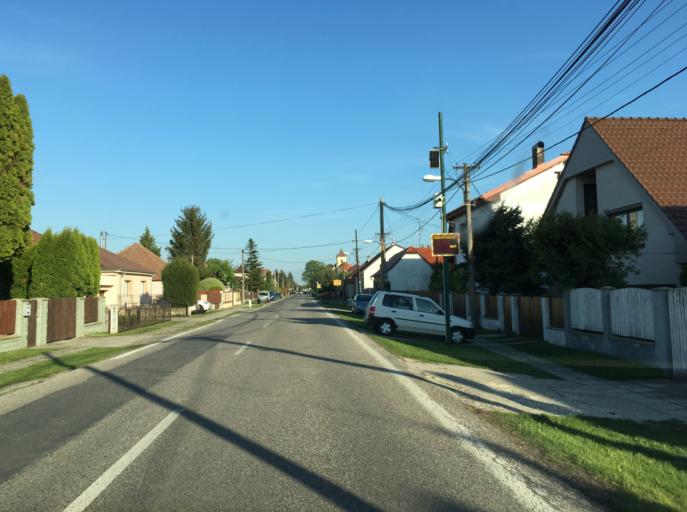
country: AT
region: Burgenland
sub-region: Politischer Bezirk Neusiedl am See
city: Kittsee
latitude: 48.0672
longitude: 17.1074
